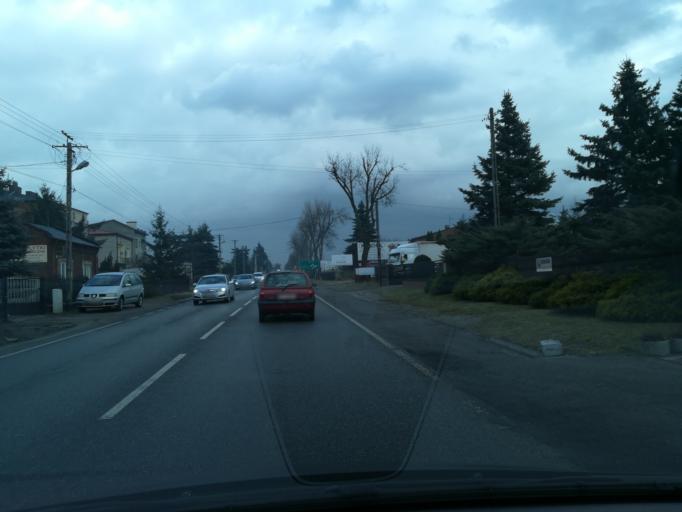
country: PL
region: Lodz Voivodeship
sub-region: Powiat radomszczanski
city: Radomsko
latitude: 51.0751
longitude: 19.4071
